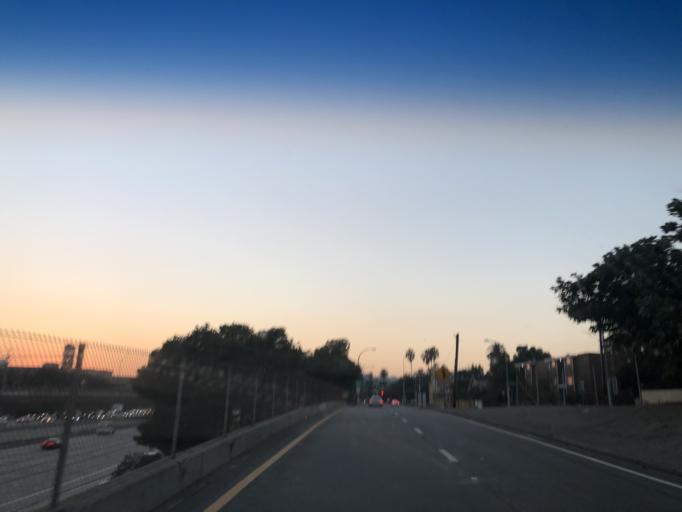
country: US
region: California
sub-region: Los Angeles County
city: Pasadena
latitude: 34.1523
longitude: -118.1437
